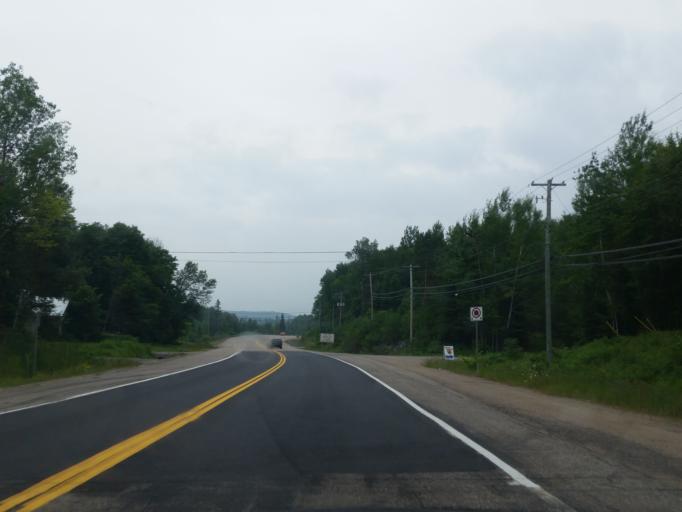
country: CA
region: Ontario
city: Huntsville
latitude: 45.3518
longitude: -79.1482
